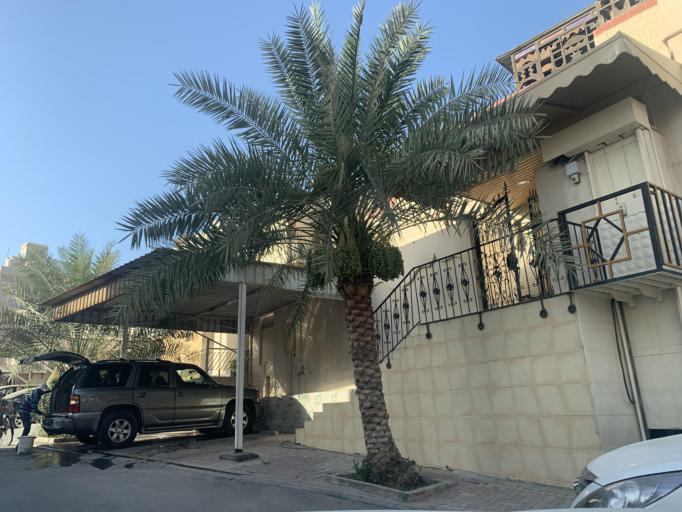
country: BH
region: Manama
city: Jidd Hafs
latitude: 26.2241
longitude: 50.5339
